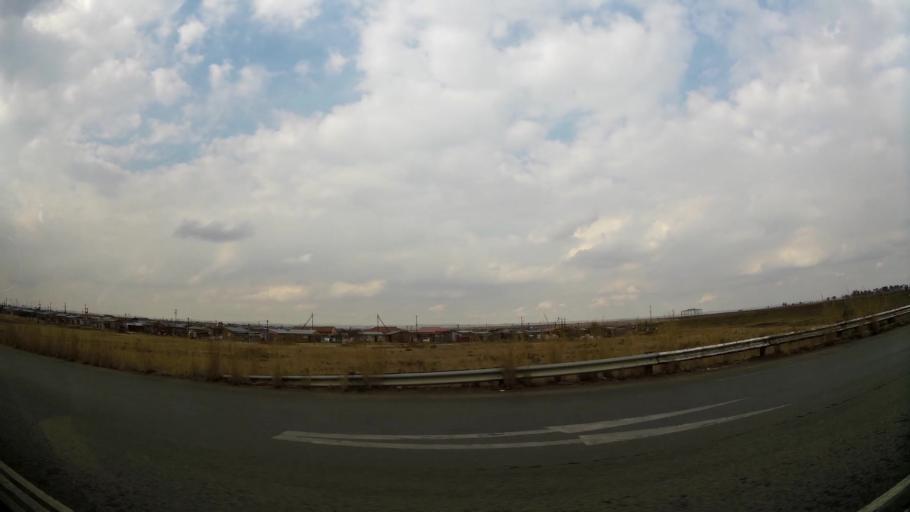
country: ZA
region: Orange Free State
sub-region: Fezile Dabi District Municipality
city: Sasolburg
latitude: -26.8644
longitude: 27.8879
